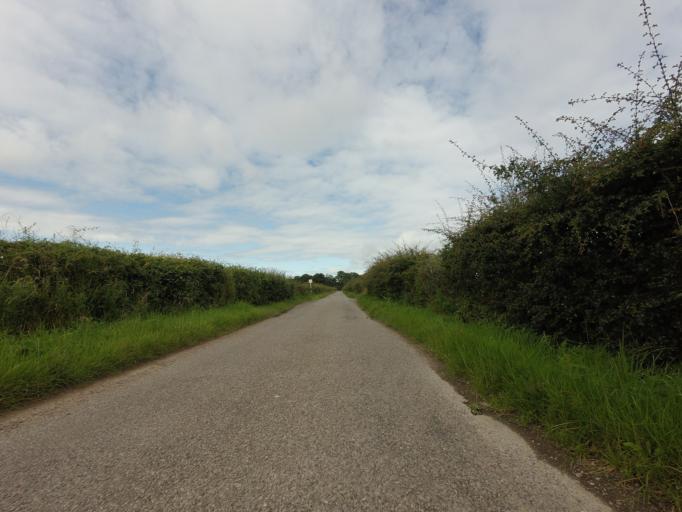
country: GB
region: Scotland
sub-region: Moray
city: Hopeman
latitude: 57.6702
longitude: -3.3920
